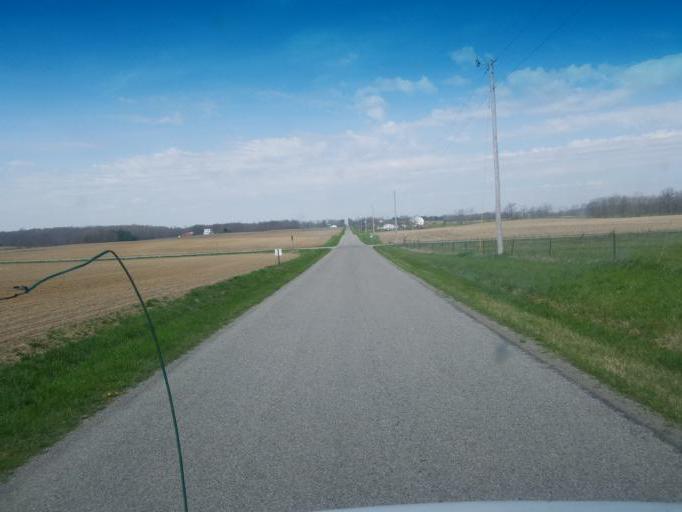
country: US
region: Ohio
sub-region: Logan County
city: Northwood
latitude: 40.4984
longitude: -83.6570
